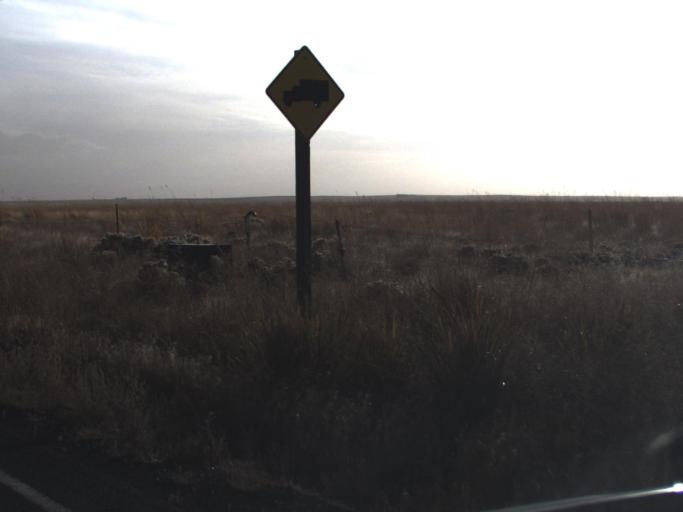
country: US
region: Washington
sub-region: Adams County
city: Ritzville
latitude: 47.3184
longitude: -118.6904
